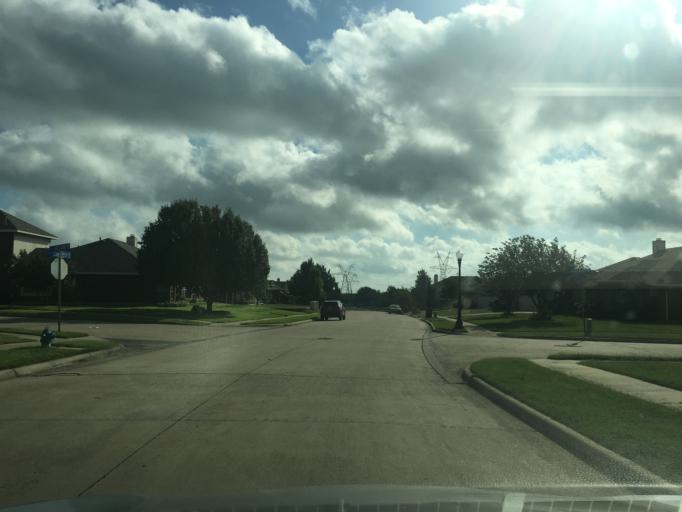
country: US
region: Texas
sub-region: Dallas County
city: Sachse
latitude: 32.9667
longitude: -96.5890
